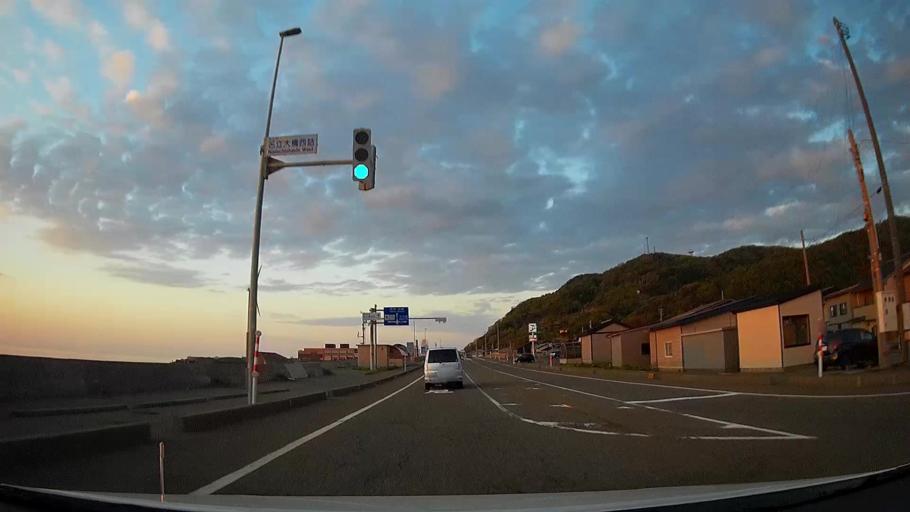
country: JP
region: Niigata
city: Joetsu
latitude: 37.1594
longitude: 138.0841
